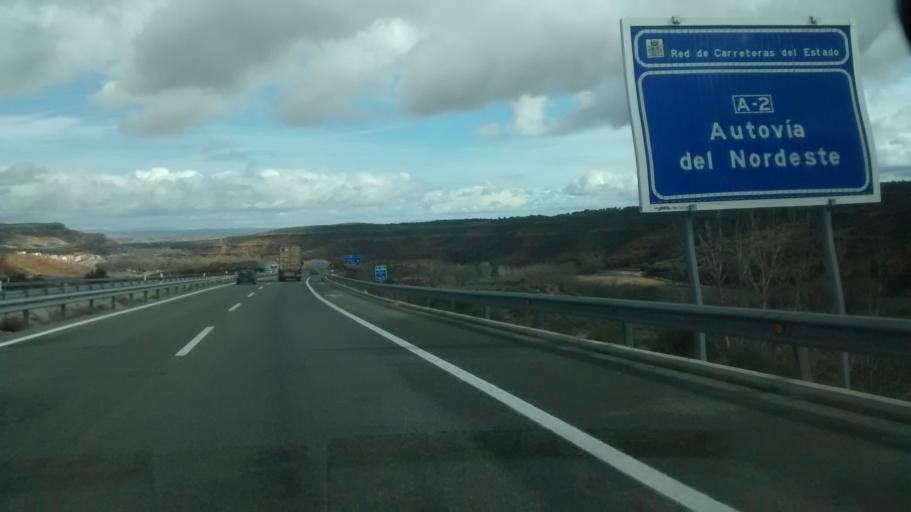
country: ES
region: Castille and Leon
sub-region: Provincia de Soria
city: Arcos de Jalon
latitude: 41.2028
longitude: -2.3010
